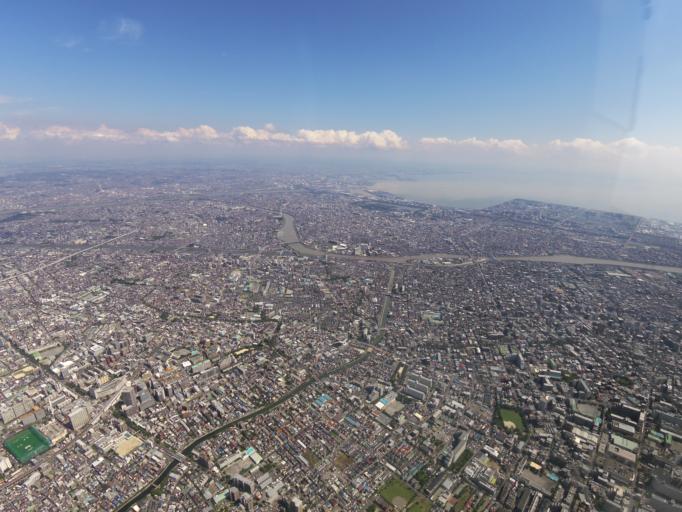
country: JP
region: Tokyo
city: Urayasu
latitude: 35.6760
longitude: 139.8533
